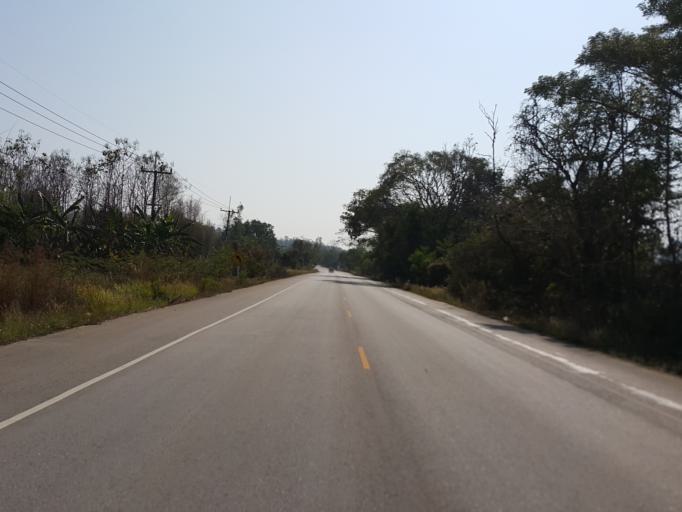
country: TH
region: Lampang
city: Chae Hom
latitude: 18.7905
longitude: 99.5857
